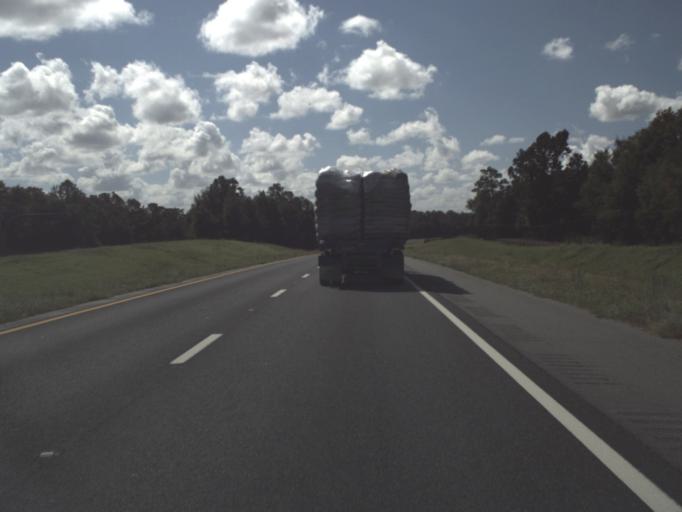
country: US
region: Florida
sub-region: Hernando County
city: Brookridge
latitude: 28.6343
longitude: -82.4896
